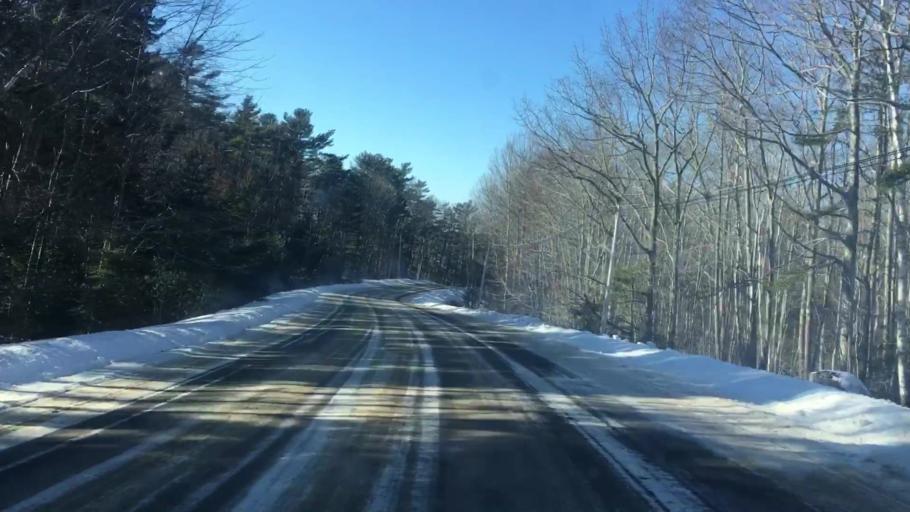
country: US
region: Maine
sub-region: Hancock County
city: Sedgwick
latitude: 44.3436
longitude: -68.6765
